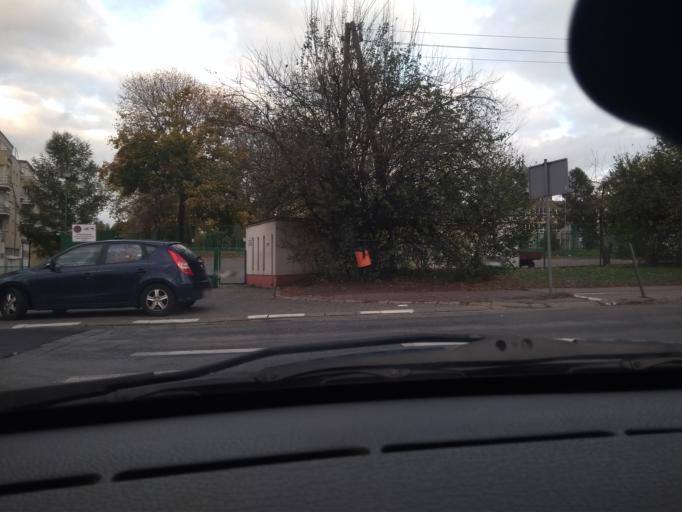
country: PL
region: Greater Poland Voivodeship
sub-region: Poznan
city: Poznan
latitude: 52.4280
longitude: 16.9260
